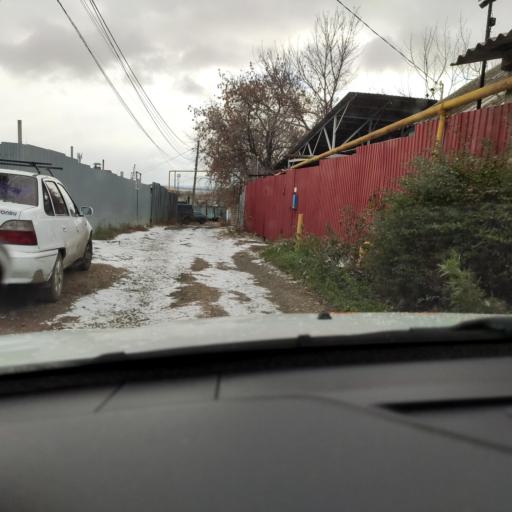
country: RU
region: Samara
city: Samara
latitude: 53.1789
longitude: 50.1541
